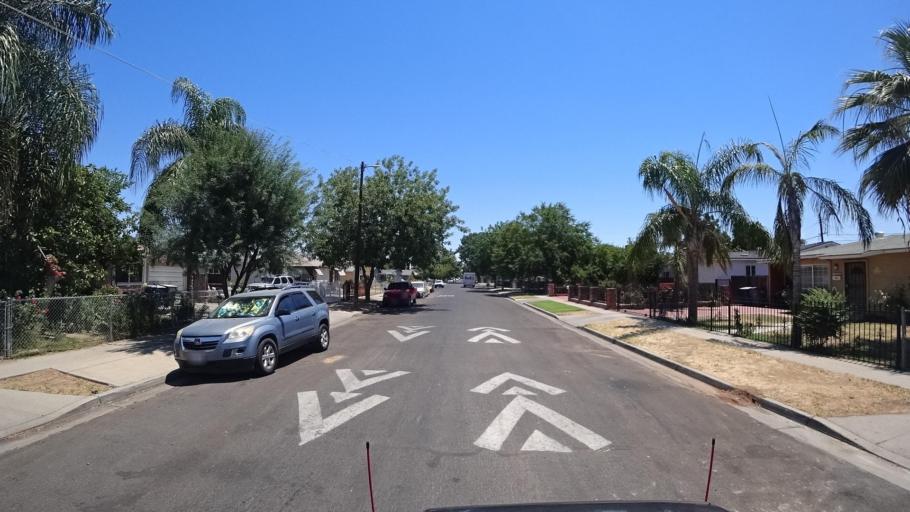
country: US
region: California
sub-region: Fresno County
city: Fresno
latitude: 36.7341
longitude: -119.7422
